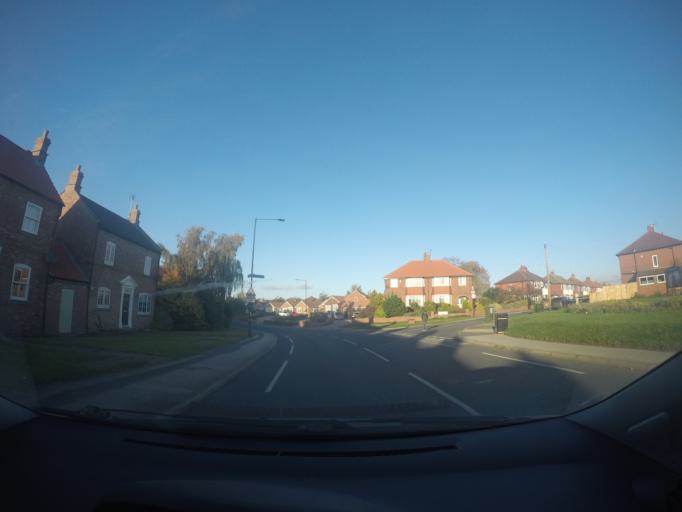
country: GB
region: England
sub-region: City of York
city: Huntington
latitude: 53.9808
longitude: -1.0675
